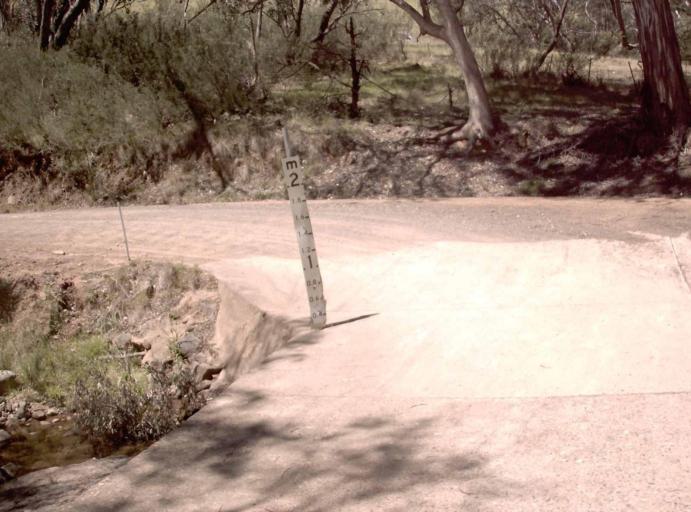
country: AU
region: New South Wales
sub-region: Snowy River
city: Jindabyne
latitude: -37.0766
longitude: 148.4943
